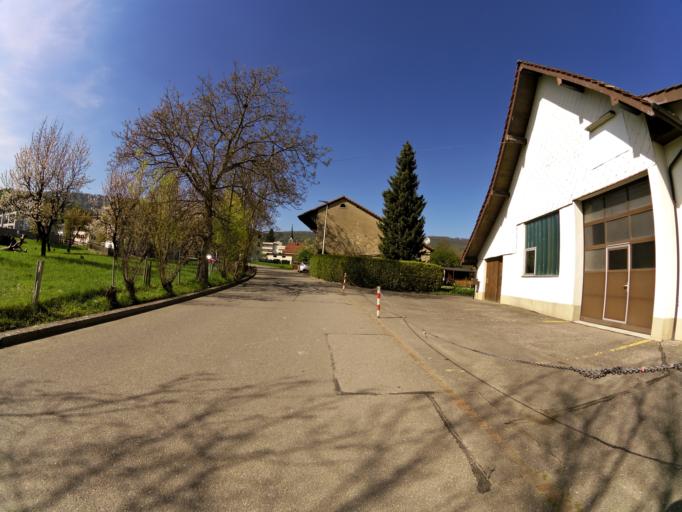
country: CH
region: Solothurn
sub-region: Bezirk Goesgen
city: Niedererlinsbach
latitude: 47.3932
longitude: 8.0091
